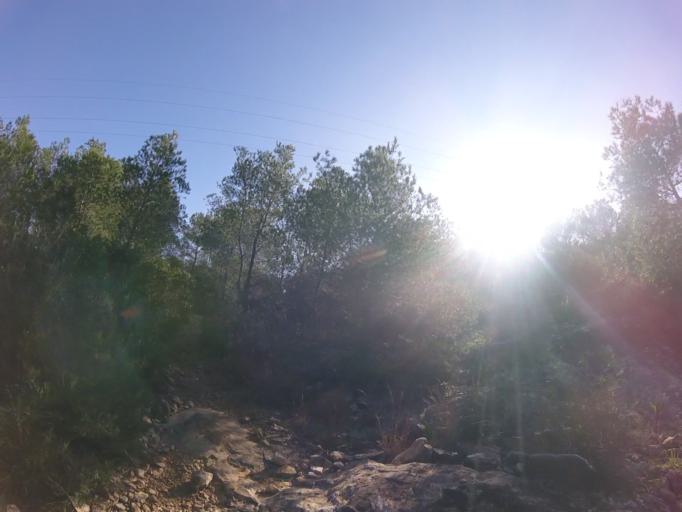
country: ES
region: Valencia
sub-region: Provincia de Castello
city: Santa Magdalena de Pulpis
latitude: 40.3005
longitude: 0.3310
